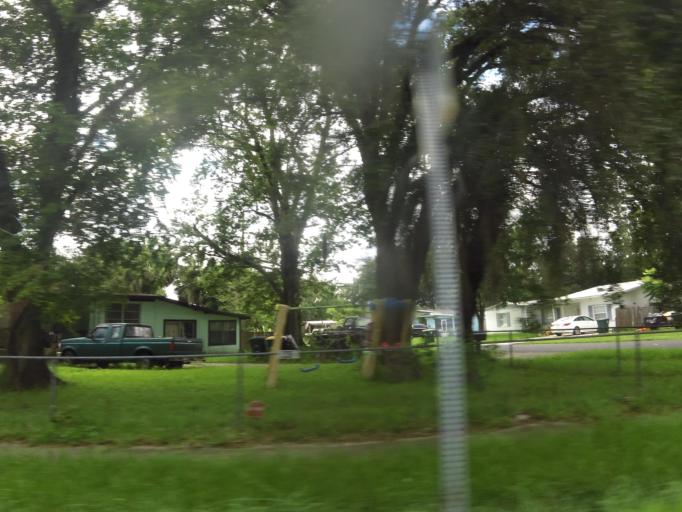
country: US
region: Florida
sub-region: Duval County
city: Jacksonville
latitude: 30.2835
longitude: -81.5542
